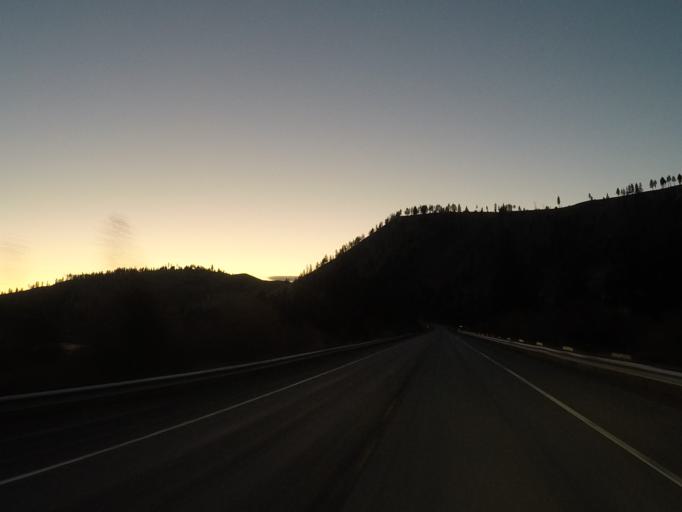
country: US
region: Montana
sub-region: Missoula County
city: Seeley Lake
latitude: 47.0234
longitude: -113.2989
